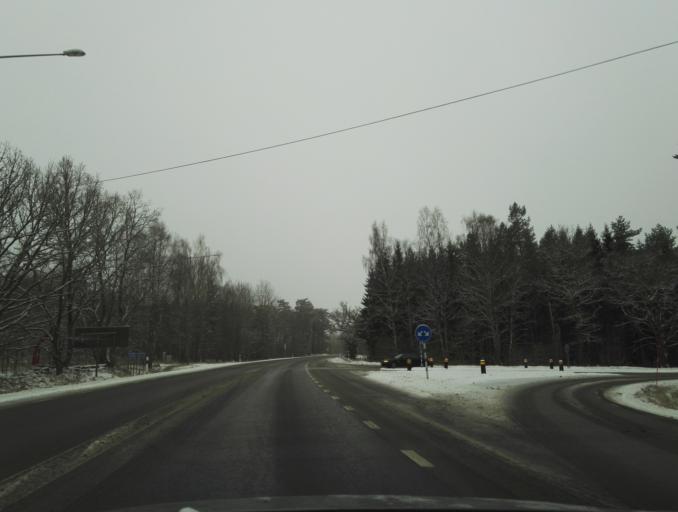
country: SE
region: Kronoberg
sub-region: Vaxjo Kommun
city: Vaexjoe
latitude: 56.8564
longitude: 14.7308
